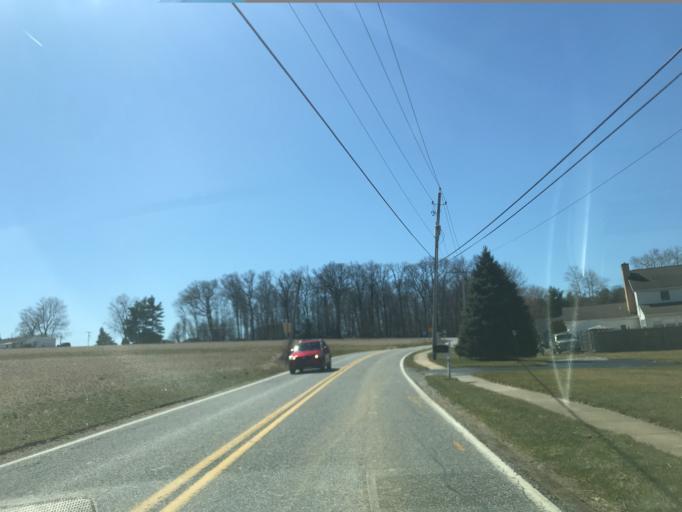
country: US
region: Pennsylvania
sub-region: York County
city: Shrewsbury
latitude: 39.7427
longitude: -76.6734
